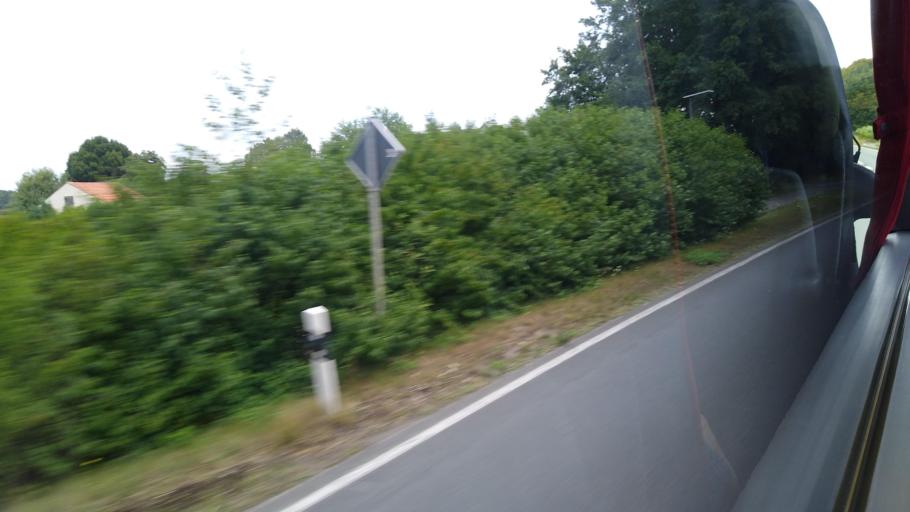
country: DE
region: North Rhine-Westphalia
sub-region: Regierungsbezirk Detmold
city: Verl
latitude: 51.8553
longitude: 8.5745
